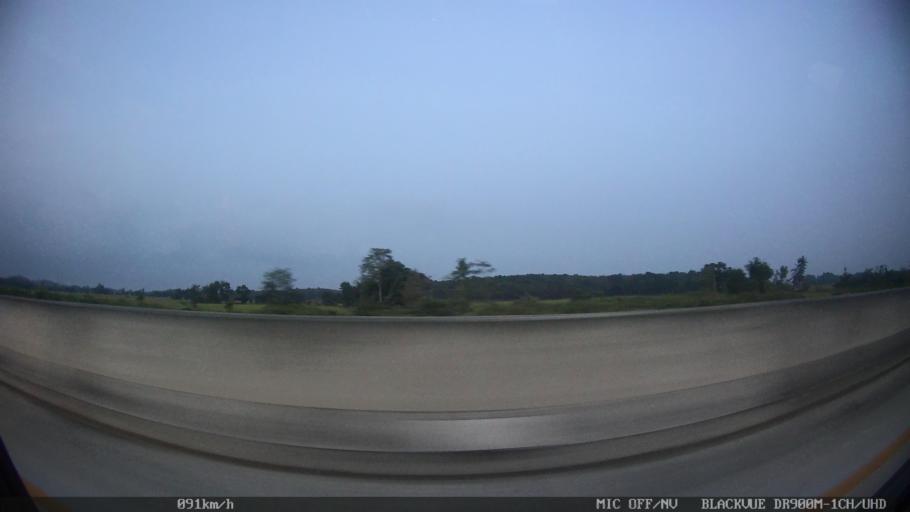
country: ID
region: Lampung
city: Sidorejo
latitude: -5.5802
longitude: 105.5423
